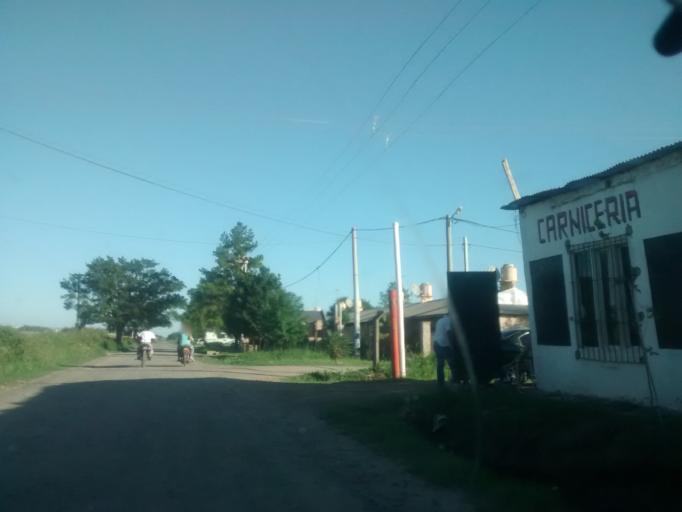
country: AR
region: Chaco
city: Fontana
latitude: -27.4593
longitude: -59.0348
